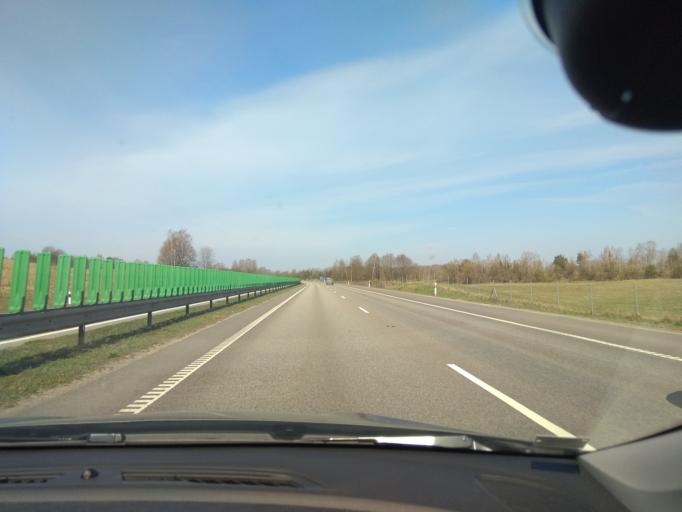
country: LT
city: Trakai
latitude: 54.7389
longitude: 24.9488
